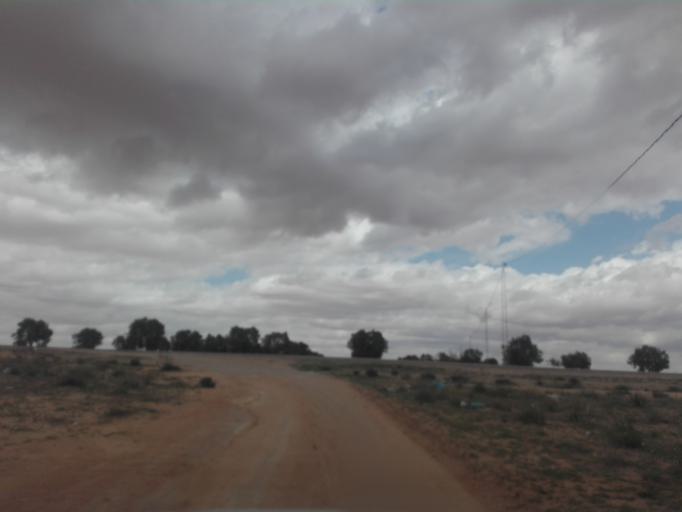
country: TN
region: Safaqis
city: Sfax
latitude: 34.7283
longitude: 10.4313
